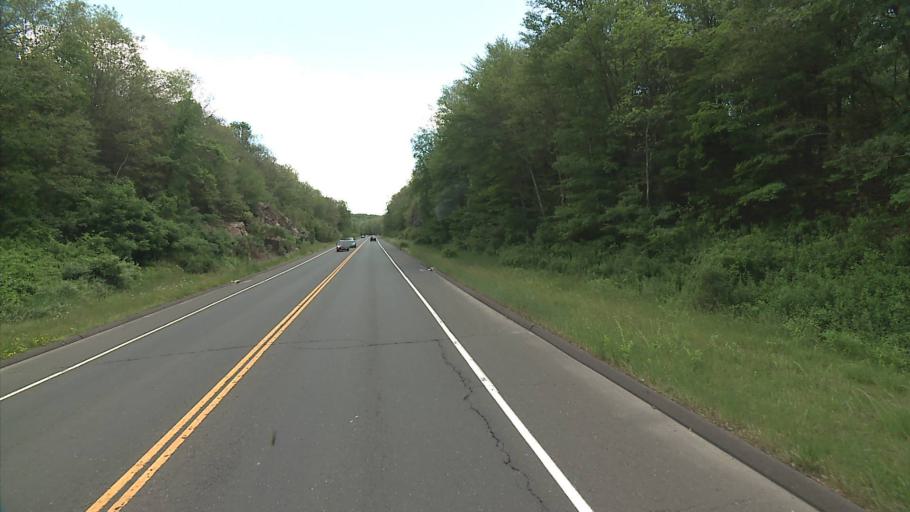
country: US
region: Connecticut
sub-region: New Haven County
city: Naugatuck
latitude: 41.5188
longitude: -73.0786
